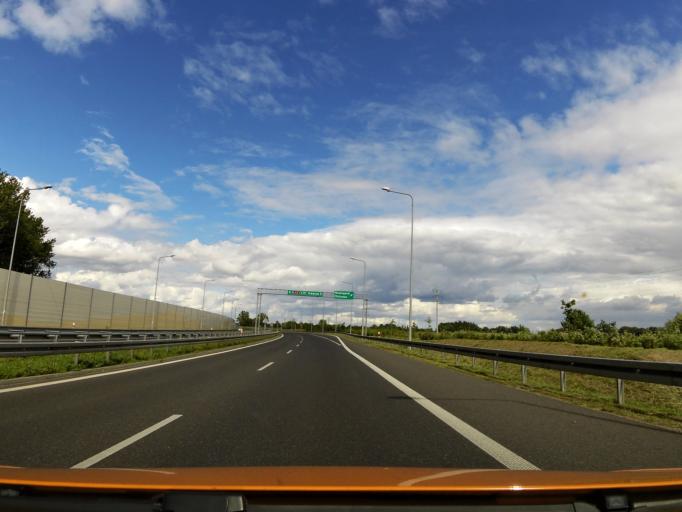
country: PL
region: West Pomeranian Voivodeship
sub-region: Powiat goleniowski
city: Nowogard
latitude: 53.6513
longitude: 15.0734
